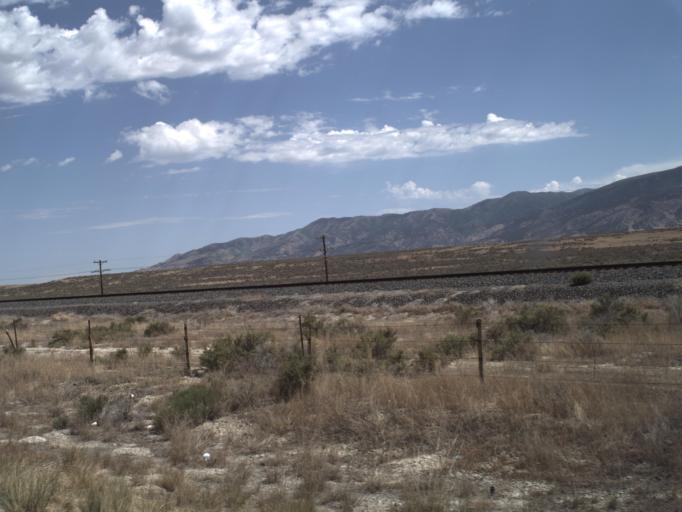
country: US
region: Utah
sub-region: Tooele County
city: Tooele
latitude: 40.3401
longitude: -112.4101
